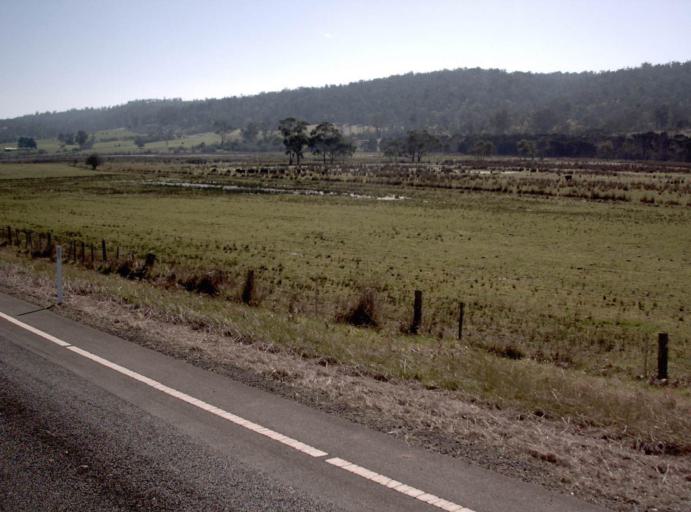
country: AU
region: Tasmania
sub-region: Launceston
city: Mayfield
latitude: -41.3241
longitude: 147.0633
